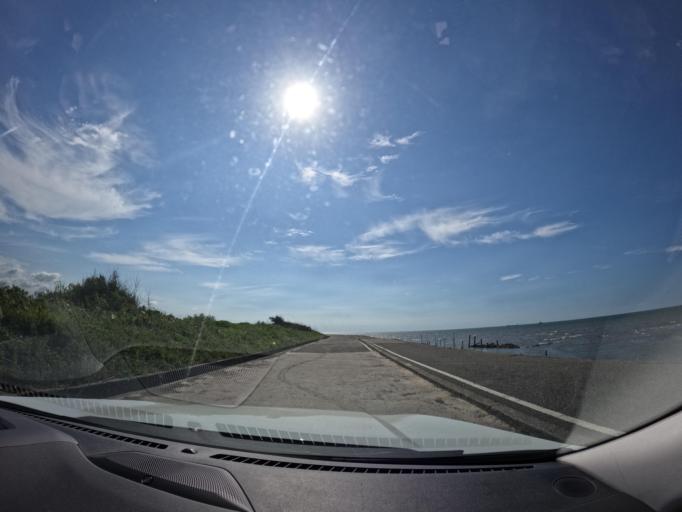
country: TW
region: Taiwan
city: Taoyuan City
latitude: 25.0936
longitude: 121.1872
